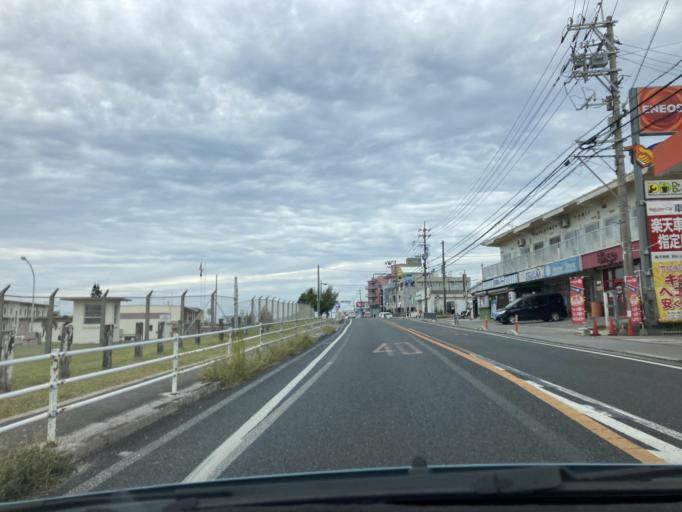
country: JP
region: Okinawa
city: Okinawa
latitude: 26.3842
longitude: 127.7411
